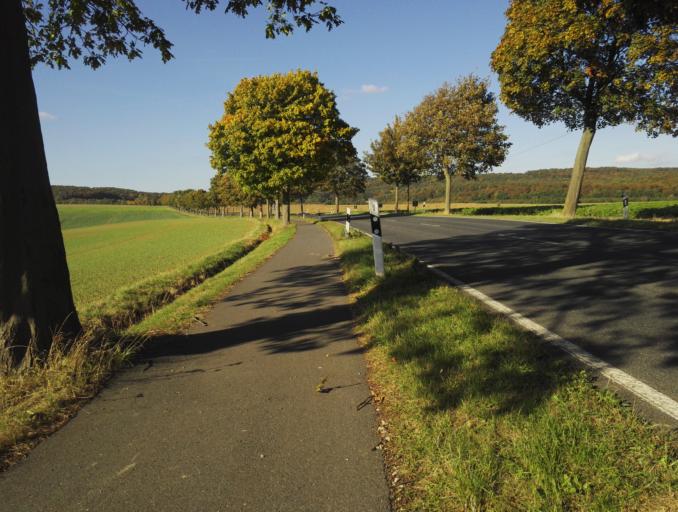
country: DE
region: Lower Saxony
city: Holle
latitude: 52.1116
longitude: 10.1069
